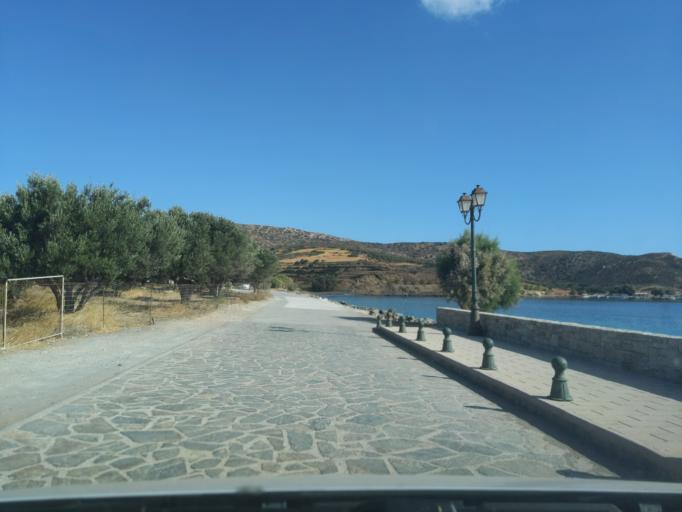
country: GR
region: Crete
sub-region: Nomos Lasithiou
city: Palekastro
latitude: 35.2132
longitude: 26.2675
